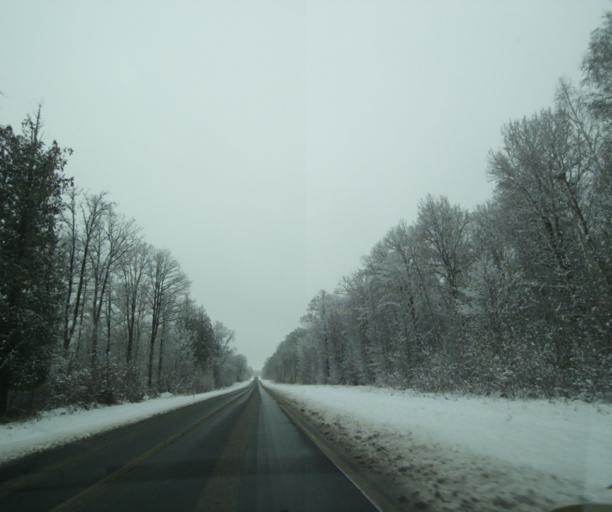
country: FR
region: Champagne-Ardenne
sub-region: Departement de la Haute-Marne
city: Laneuville-a-Remy
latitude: 48.5567
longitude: 4.8393
